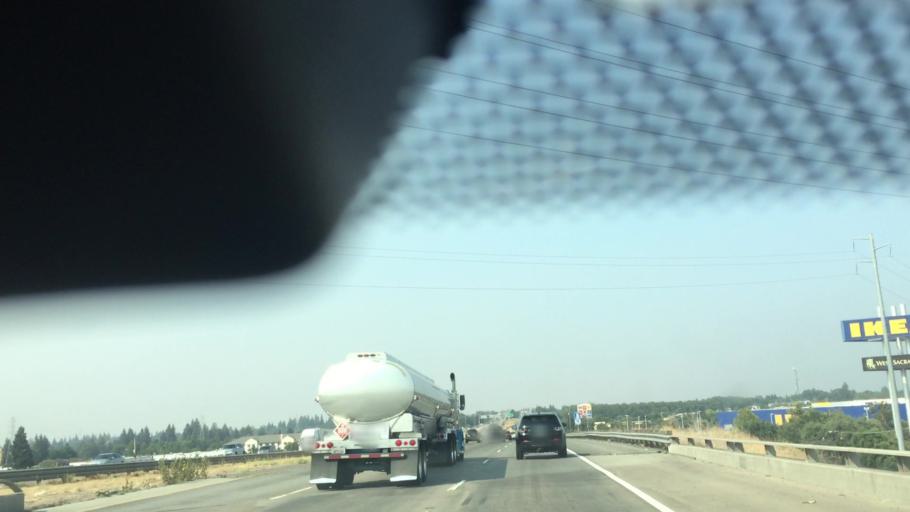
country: US
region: California
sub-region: Yolo County
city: West Sacramento
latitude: 38.5840
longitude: -121.5564
